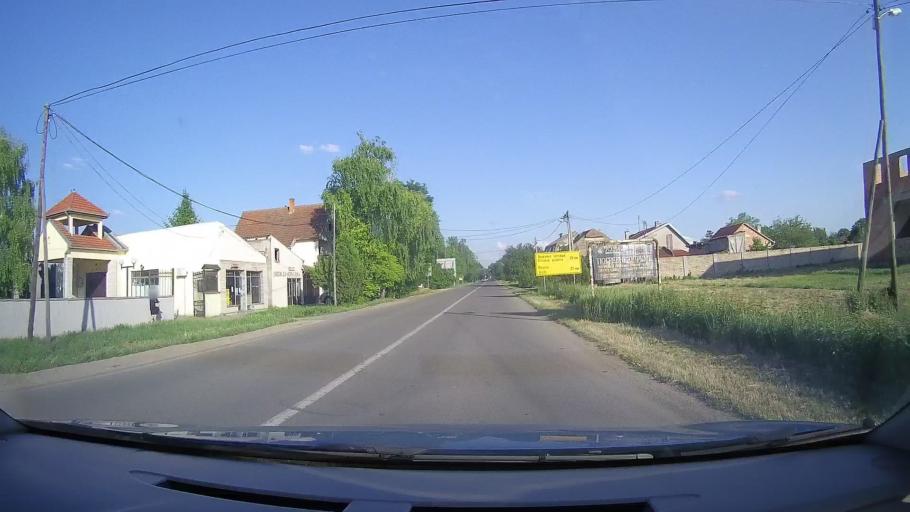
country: RS
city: Banatski Karlovac
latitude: 45.0531
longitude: 21.0086
